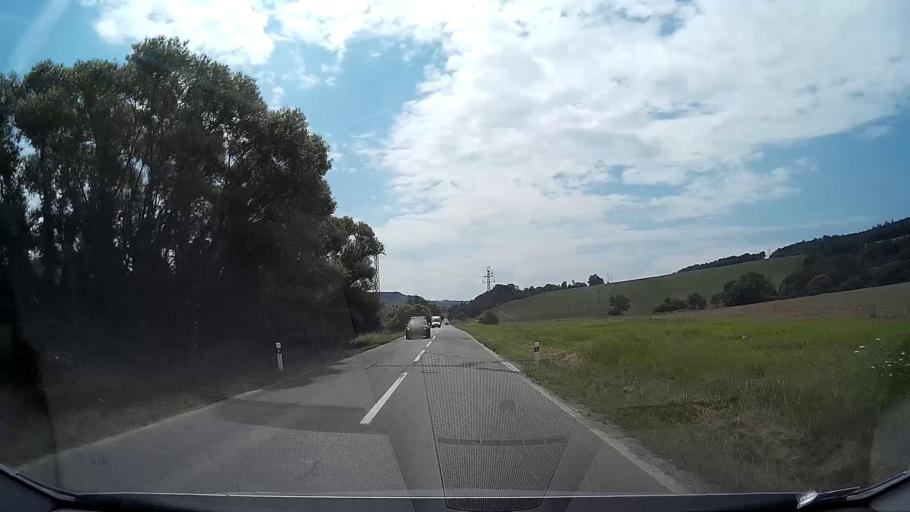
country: SK
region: Banskobystricky
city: Tisovec
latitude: 48.5497
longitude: 19.9587
